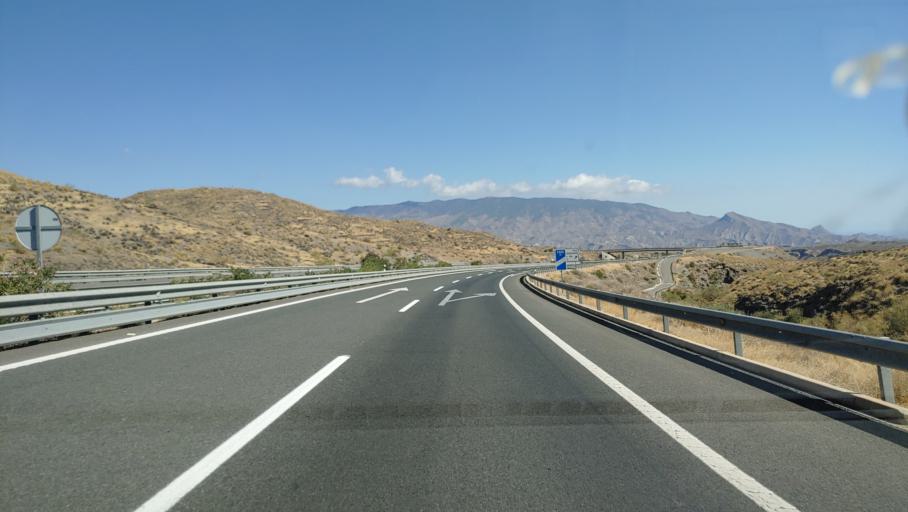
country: ES
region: Andalusia
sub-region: Provincia de Almeria
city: Gergal
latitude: 37.0704
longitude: -2.4939
